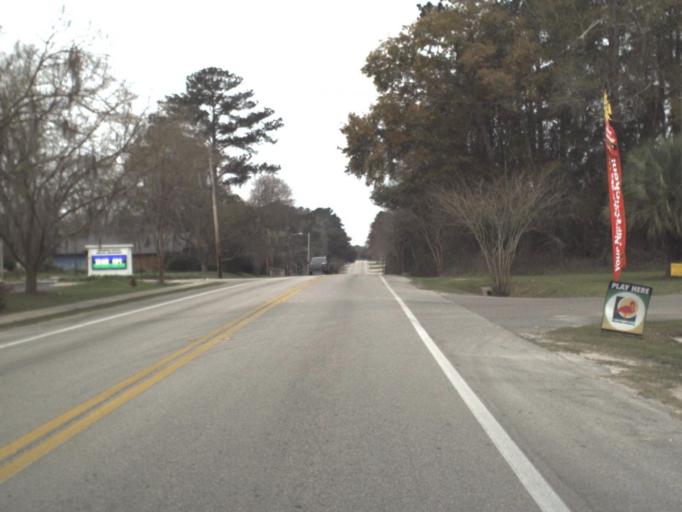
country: US
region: Florida
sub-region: Jefferson County
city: Monticello
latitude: 30.5450
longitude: -83.8813
